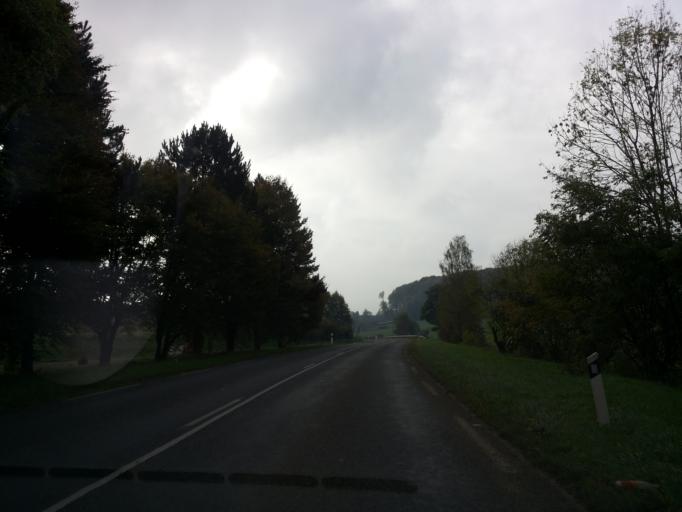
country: FR
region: Lorraine
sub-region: Departement de la Meuse
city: Montmedy
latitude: 49.4822
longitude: 5.3847
